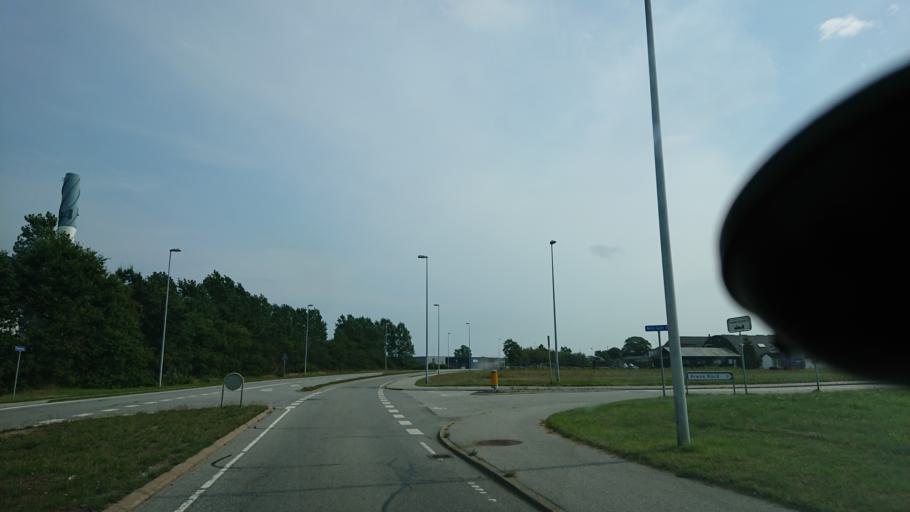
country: DK
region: North Denmark
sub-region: Frederikshavn Kommune
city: Frederikshavn
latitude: 57.4568
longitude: 10.5180
